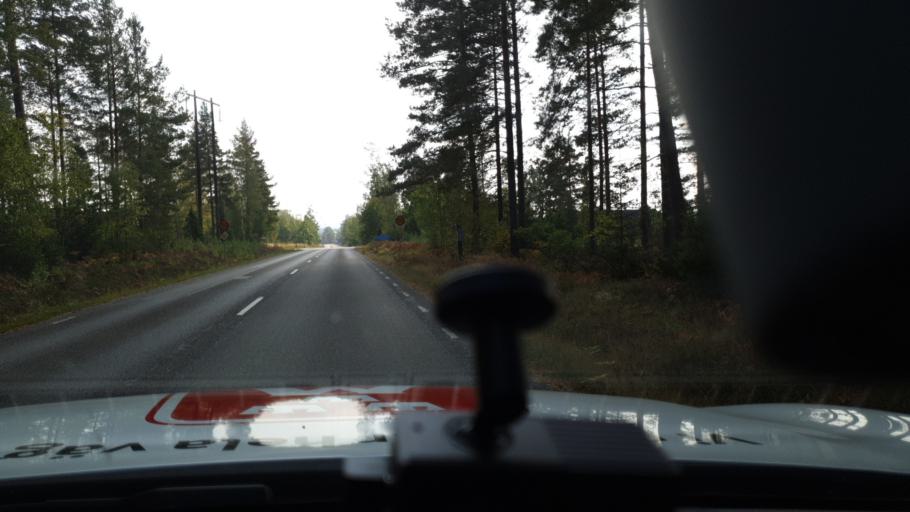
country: SE
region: Kalmar
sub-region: Vimmerby Kommun
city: Vimmerby
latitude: 57.6841
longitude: 15.8495
